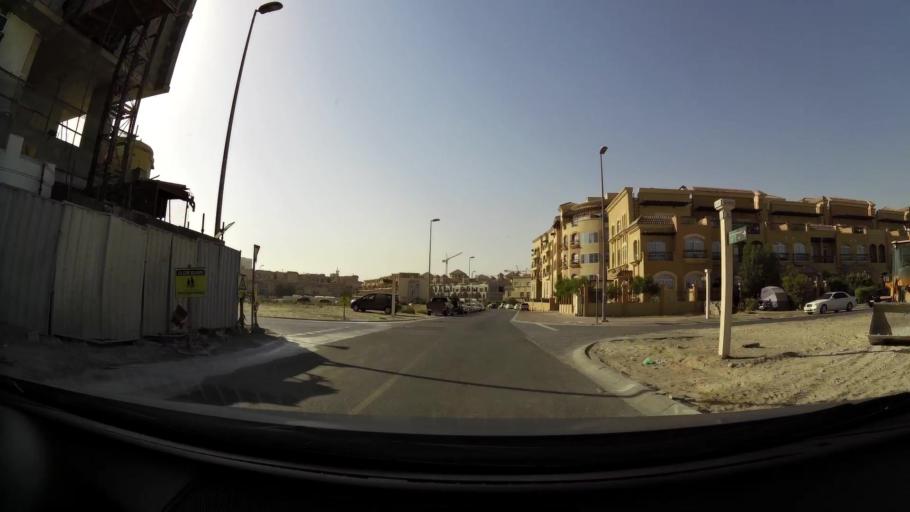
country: AE
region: Dubai
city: Dubai
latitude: 25.0610
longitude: 55.2176
